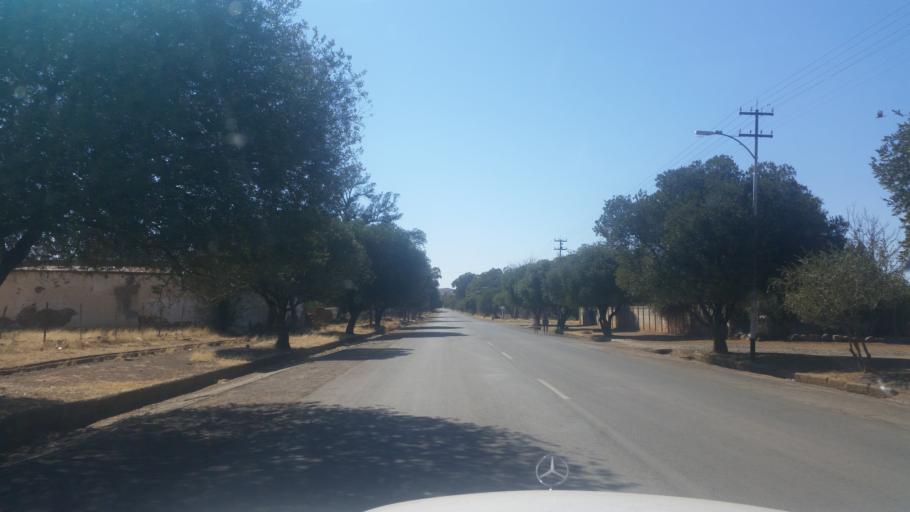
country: ZA
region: Orange Free State
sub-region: Xhariep District Municipality
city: Trompsburg
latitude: -30.4961
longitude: 25.9791
